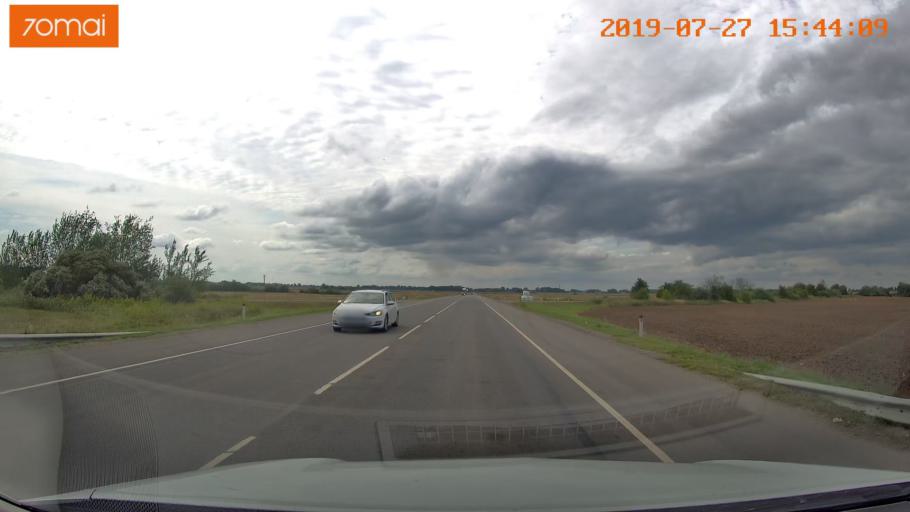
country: RU
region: Kaliningrad
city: Gusev
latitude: 54.6149
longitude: 22.1732
